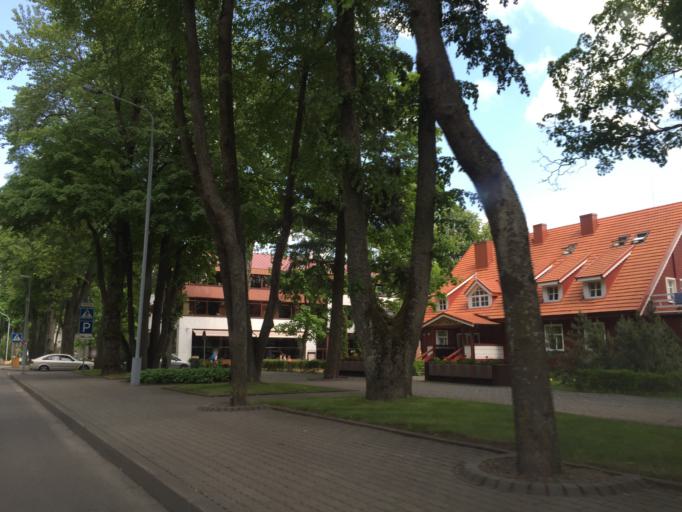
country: LT
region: Klaipedos apskritis
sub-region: Klaipeda
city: Palanga
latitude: 55.9145
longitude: 21.0647
